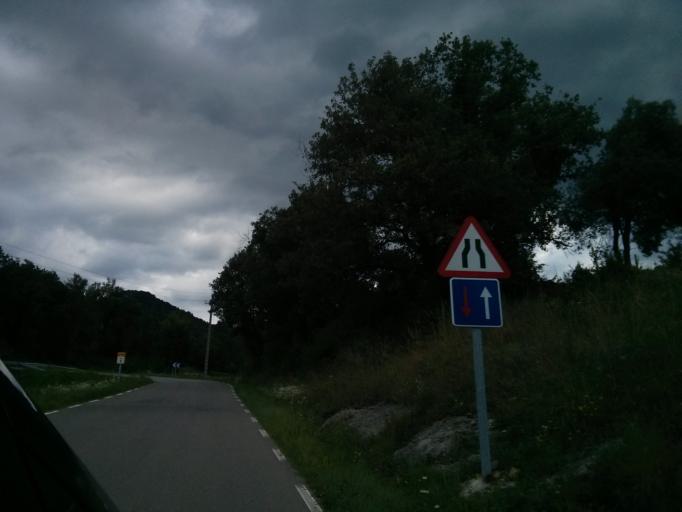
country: ES
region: Catalonia
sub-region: Provincia de Barcelona
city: Santa Maria de Corco
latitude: 42.0375
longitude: 2.3728
